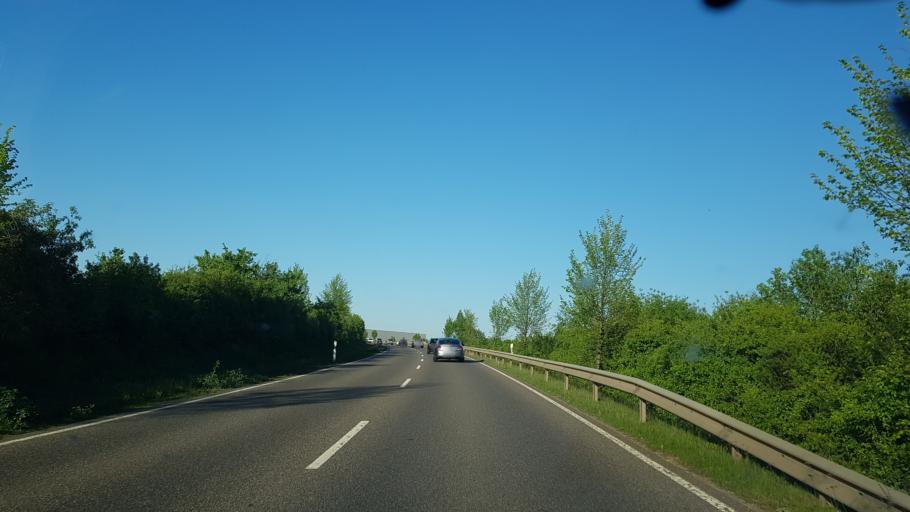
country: DE
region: North Rhine-Westphalia
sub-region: Regierungsbezirk Koln
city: Erftstadt
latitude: 50.7893
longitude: 6.7728
